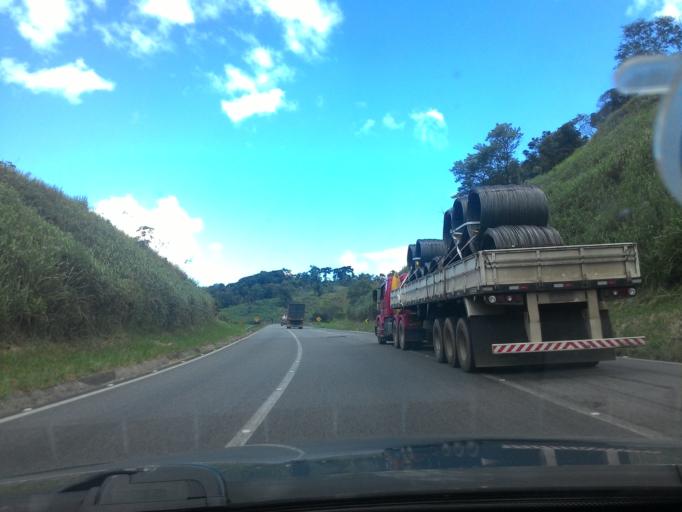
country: BR
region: Sao Paulo
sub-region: Cajati
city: Cajati
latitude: -24.7791
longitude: -48.2113
